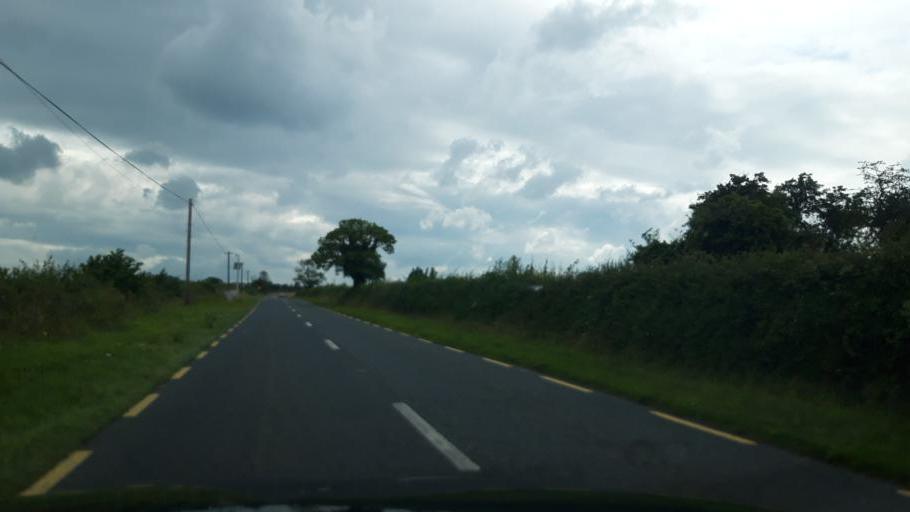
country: IE
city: Ballylinan
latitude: 52.9199
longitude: -7.0652
